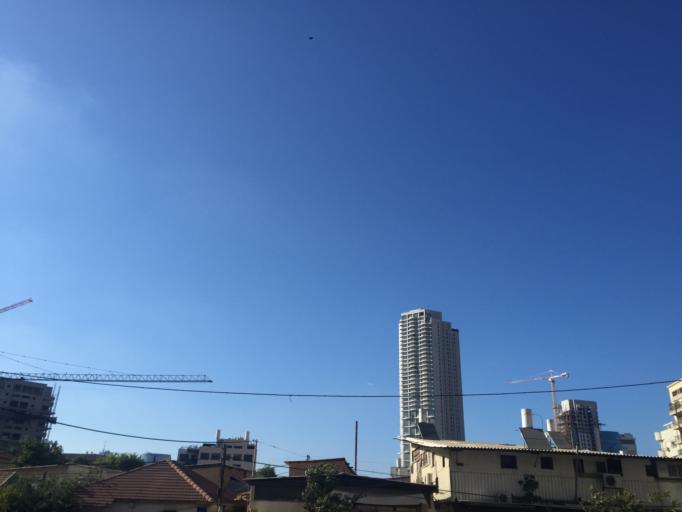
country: IL
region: Tel Aviv
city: Yafo
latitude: 32.0557
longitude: 34.7667
